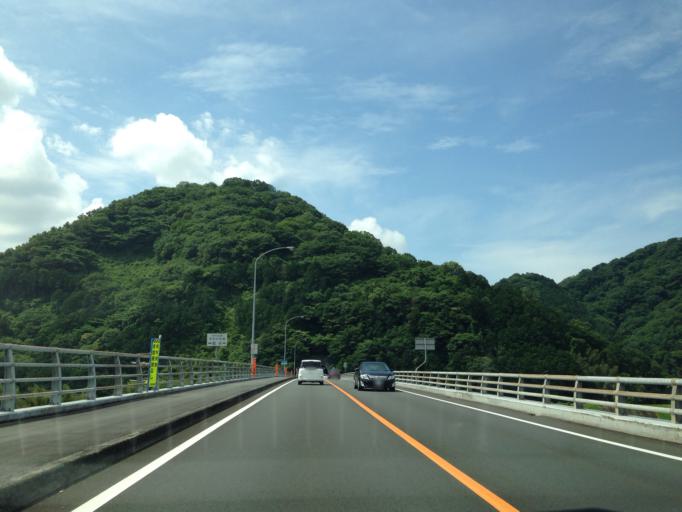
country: JP
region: Shizuoka
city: Mishima
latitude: 35.0697
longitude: 138.9250
